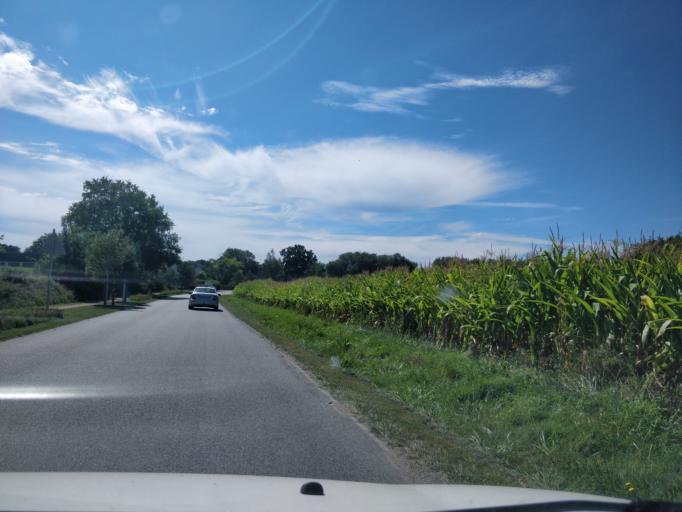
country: FR
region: Brittany
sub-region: Departement du Morbihan
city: Saint-Philibert
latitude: 47.5944
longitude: -2.9989
